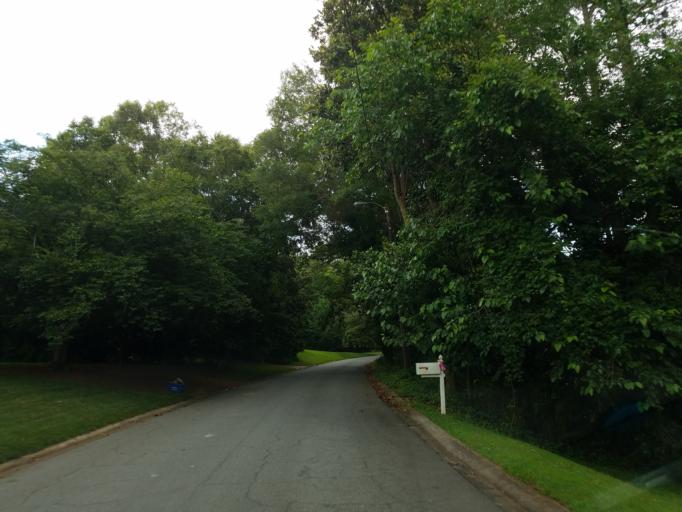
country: US
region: Georgia
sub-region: Cobb County
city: Marietta
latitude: 33.9459
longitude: -84.5619
